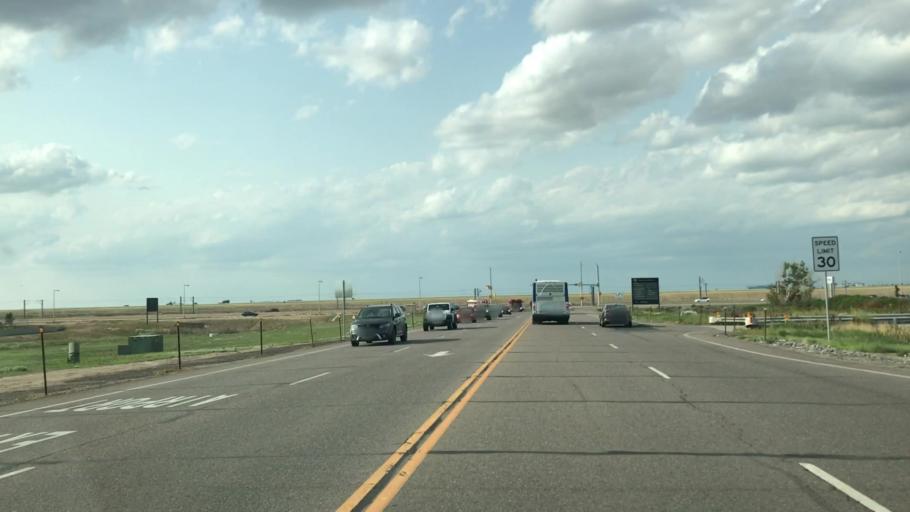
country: US
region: Colorado
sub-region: Weld County
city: Lochbuie
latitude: 39.8358
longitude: -104.6929
